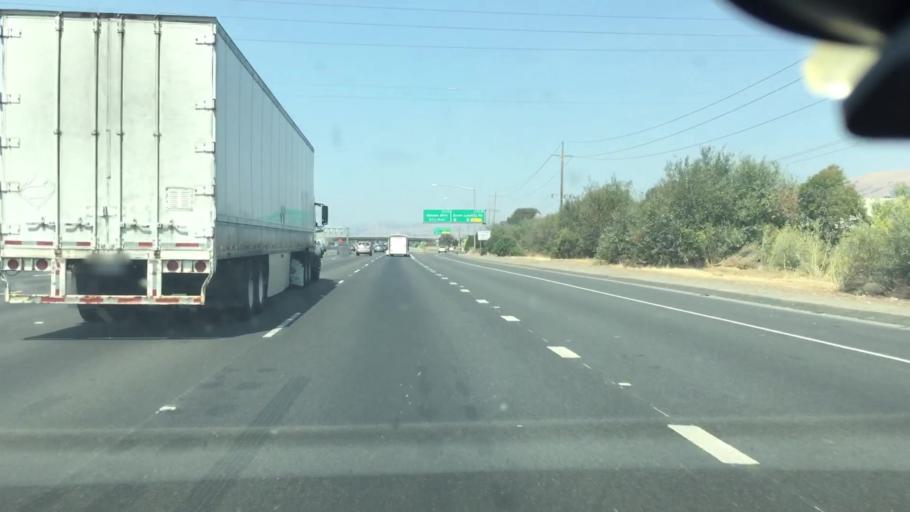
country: US
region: California
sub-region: Santa Clara County
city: Milpitas
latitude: 37.4480
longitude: -121.9204
